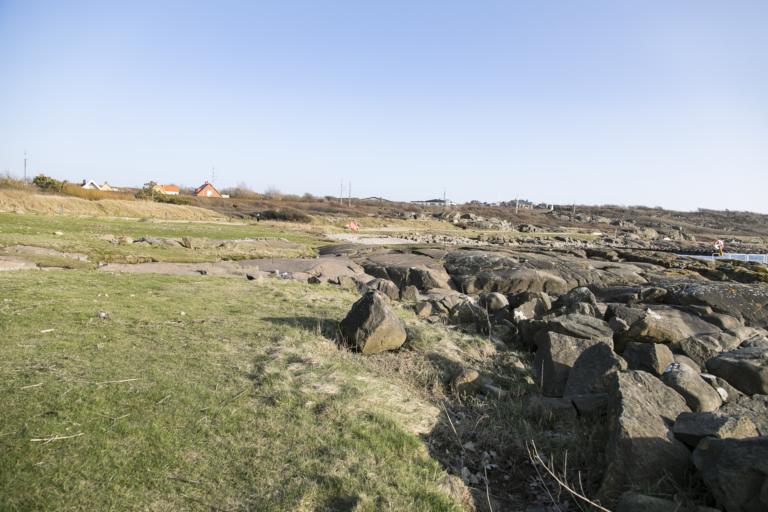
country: SE
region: Halland
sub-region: Varbergs Kommun
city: Varberg
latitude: 57.0984
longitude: 12.2425
